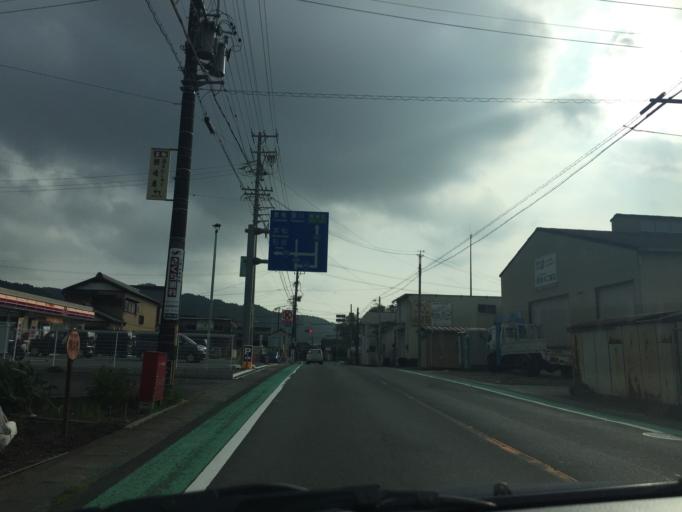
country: JP
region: Aichi
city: Shinshiro
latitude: 34.9511
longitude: 137.6060
